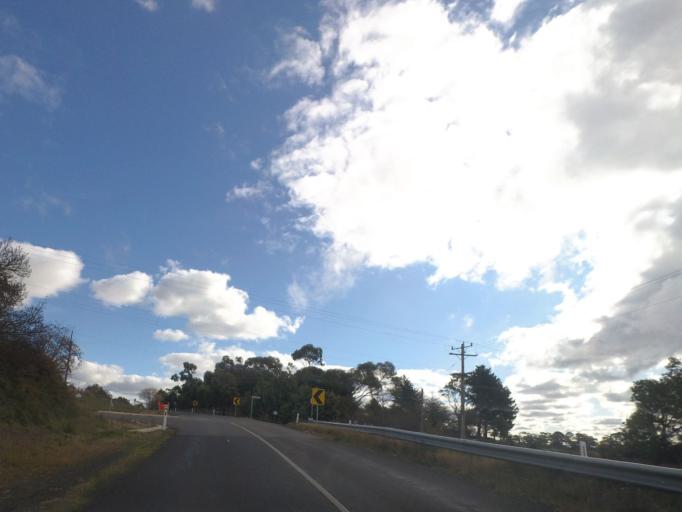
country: AU
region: Victoria
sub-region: Mount Alexander
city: Castlemaine
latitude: -37.2556
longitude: 144.4430
